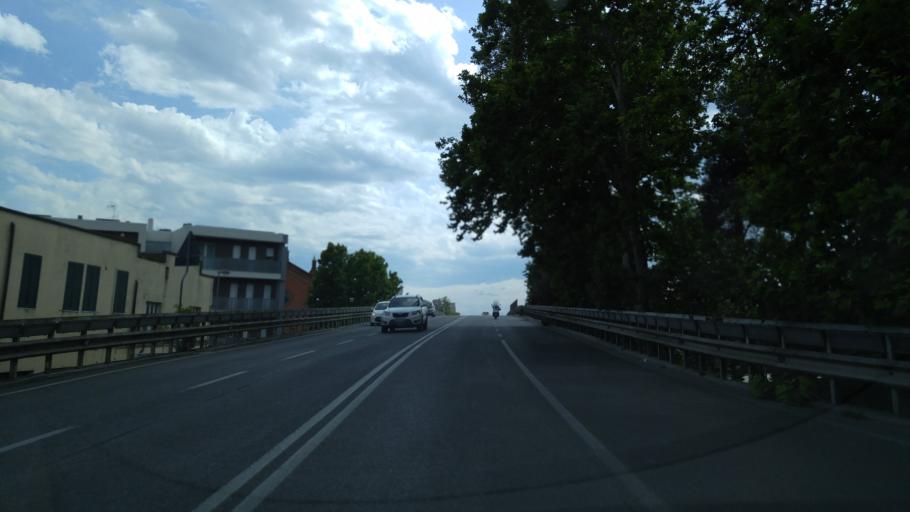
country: IT
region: The Marches
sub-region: Provincia di Pesaro e Urbino
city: Pesaro
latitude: 43.9064
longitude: 12.9080
